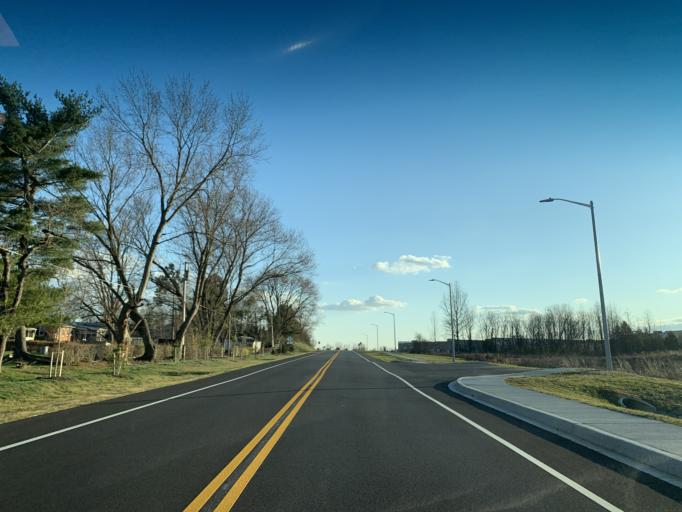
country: US
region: Maryland
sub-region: Harford County
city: Aberdeen
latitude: 39.5262
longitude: -76.1780
